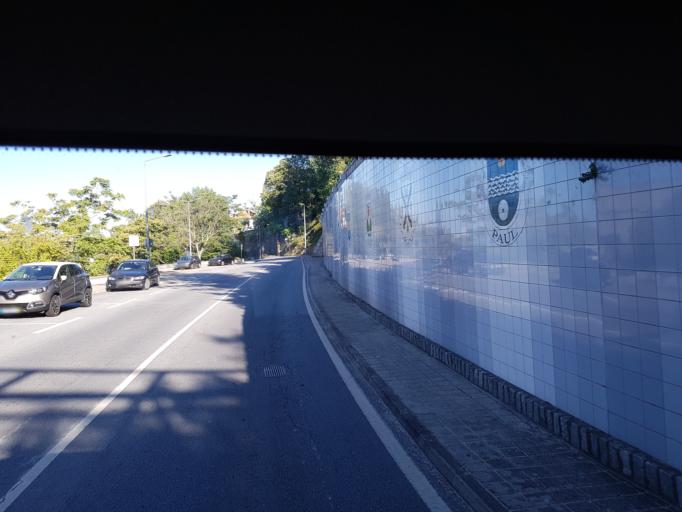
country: PT
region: Castelo Branco
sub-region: Covilha
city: Covilha
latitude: 40.2767
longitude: -7.5096
